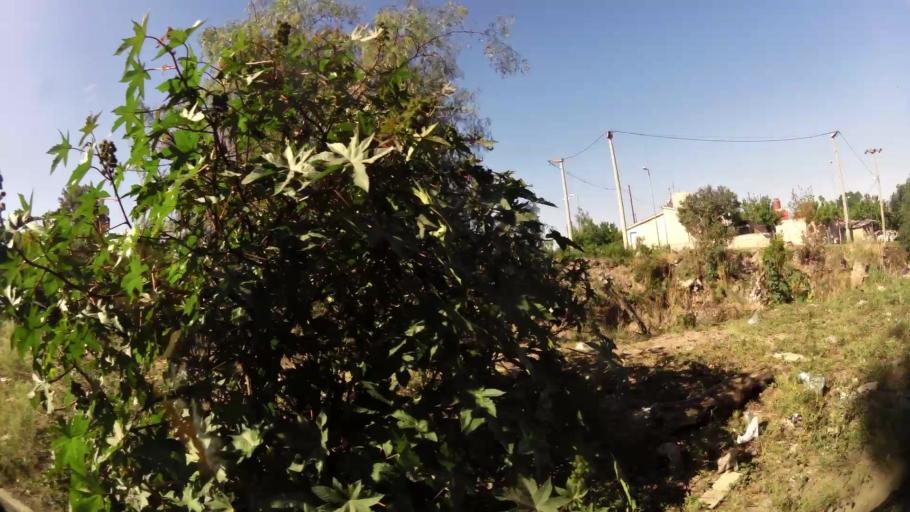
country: AR
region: Cordoba
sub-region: Departamento de Capital
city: Cordoba
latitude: -31.4028
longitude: -64.1521
